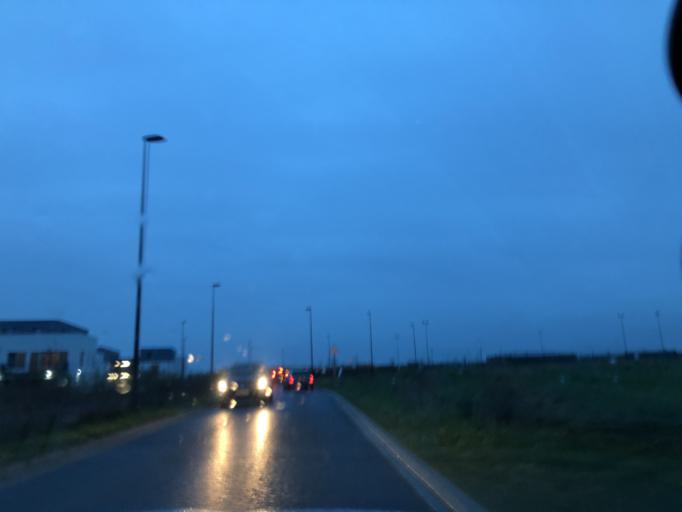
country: FR
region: Lower Normandy
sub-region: Departement du Calvados
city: Beuville
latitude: 49.2437
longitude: -0.3338
